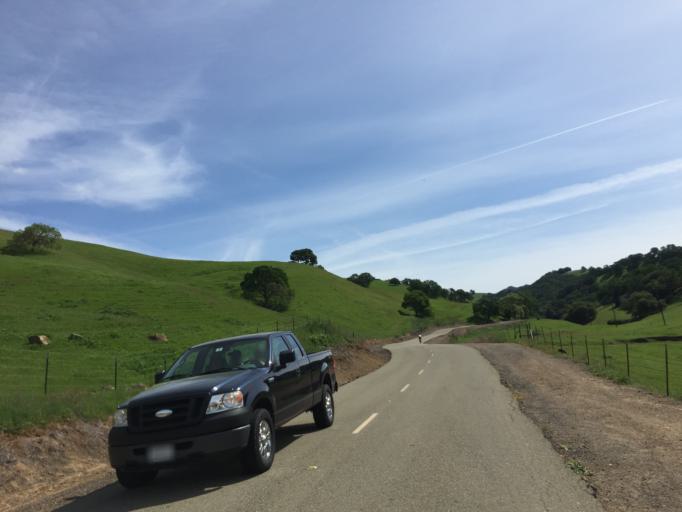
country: US
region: California
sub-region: Contra Costa County
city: Diablo
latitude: 37.8906
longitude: -121.9827
